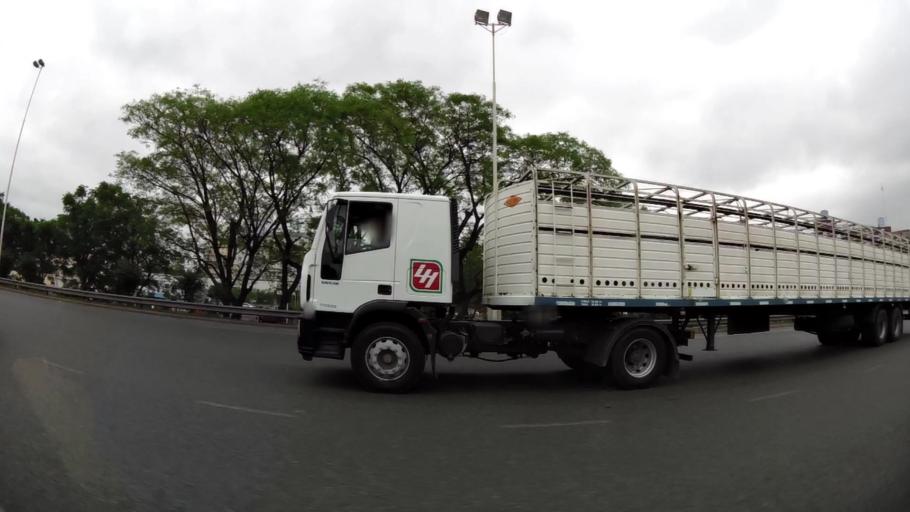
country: AR
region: Buenos Aires F.D.
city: Villa Lugano
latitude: -34.7025
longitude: -58.4984
